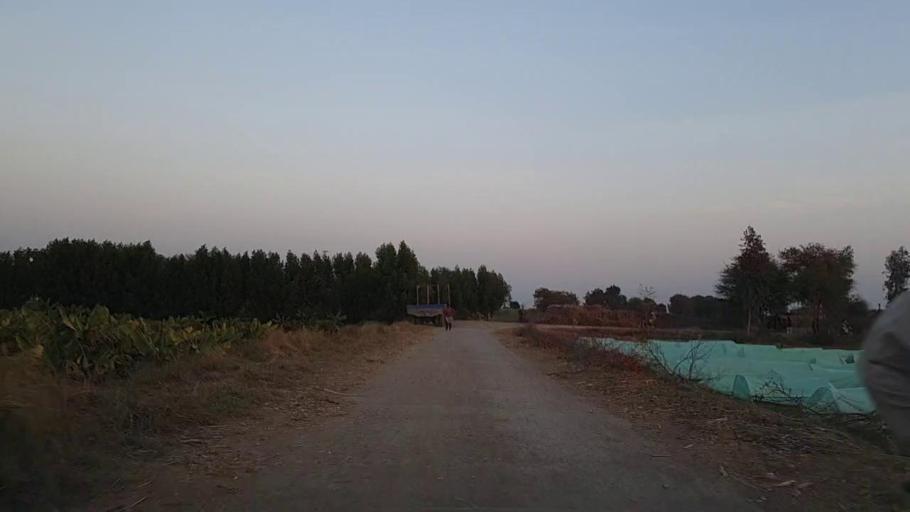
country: PK
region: Sindh
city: Tando Mittha Khan
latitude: 25.9452
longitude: 69.1539
